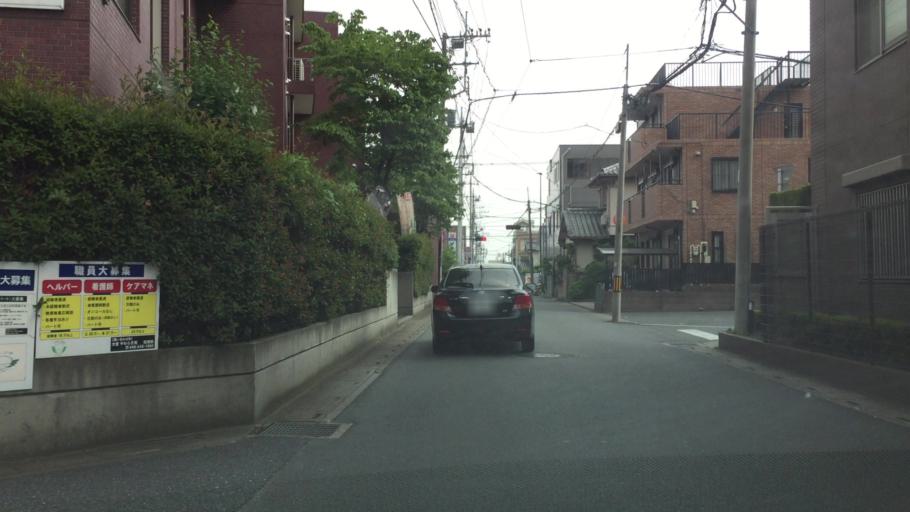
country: JP
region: Saitama
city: Yono
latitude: 35.9020
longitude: 139.6088
